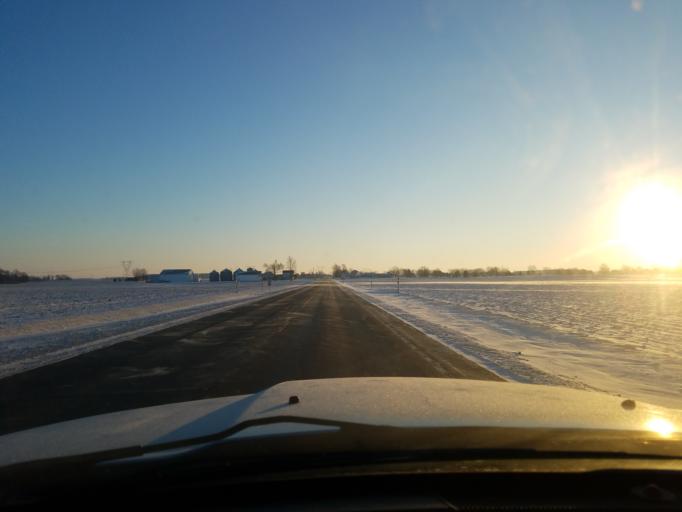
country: US
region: Indiana
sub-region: Marshall County
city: Bremen
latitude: 41.4497
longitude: -86.2517
